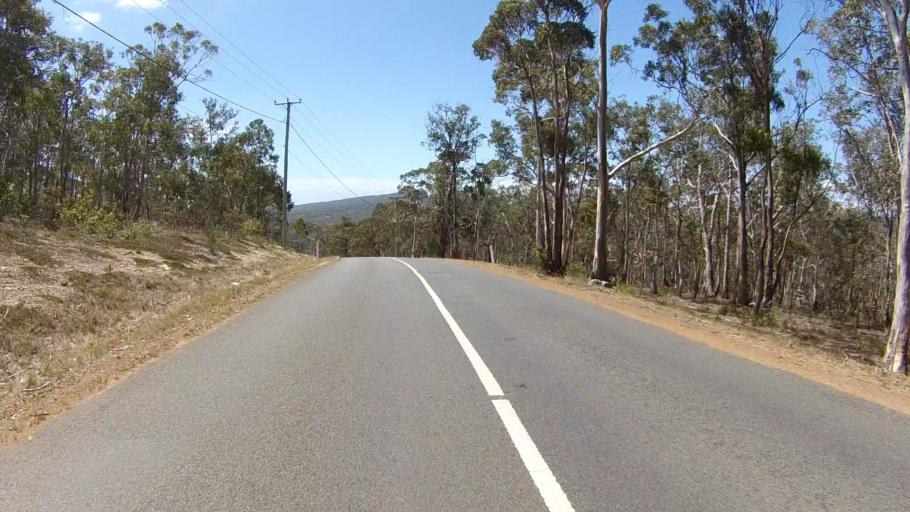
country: AU
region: Tasmania
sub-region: Clarence
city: Sandford
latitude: -42.9978
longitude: 147.4768
